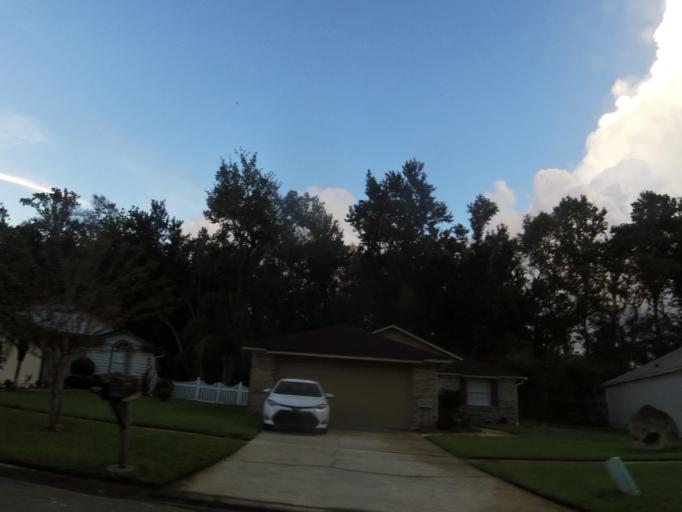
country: US
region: Florida
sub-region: Duval County
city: Jacksonville
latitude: 30.2302
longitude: -81.6030
